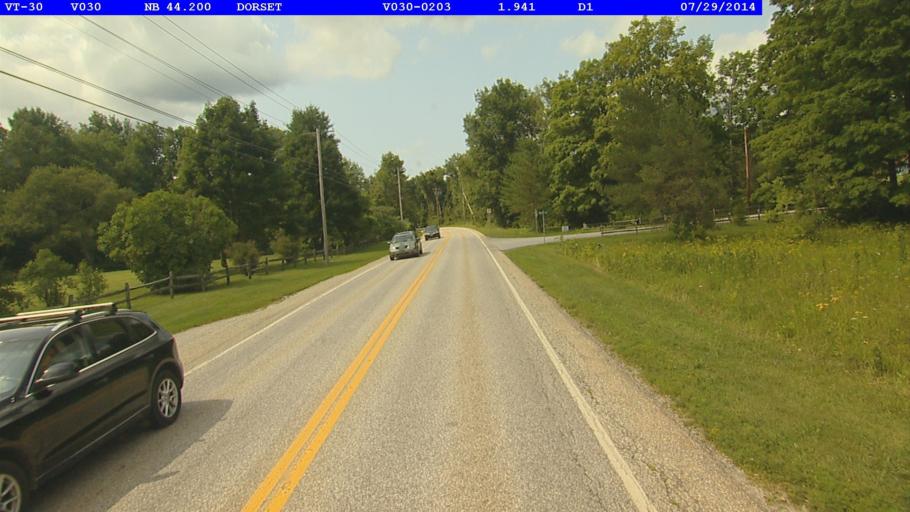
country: US
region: Vermont
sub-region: Bennington County
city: Manchester Center
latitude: 43.2372
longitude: -73.0846
